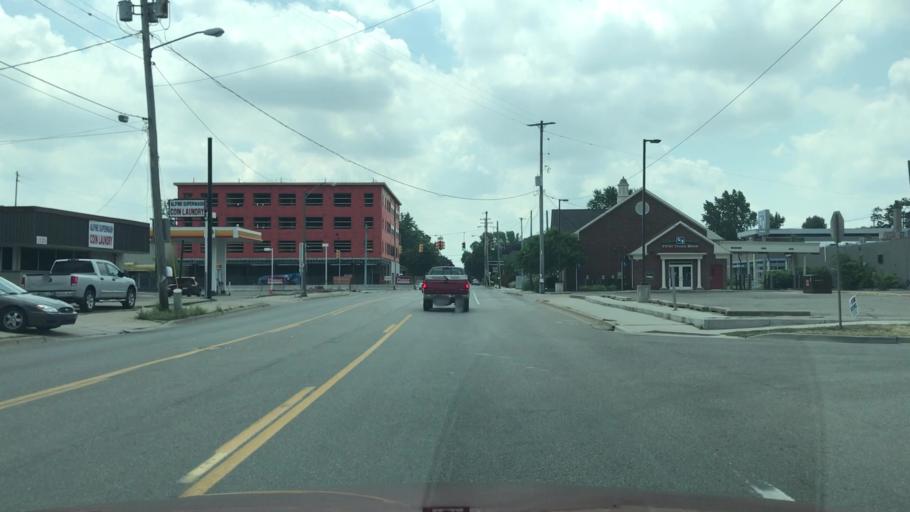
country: US
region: Michigan
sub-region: Kent County
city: Grand Rapids
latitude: 42.9863
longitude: -85.6881
